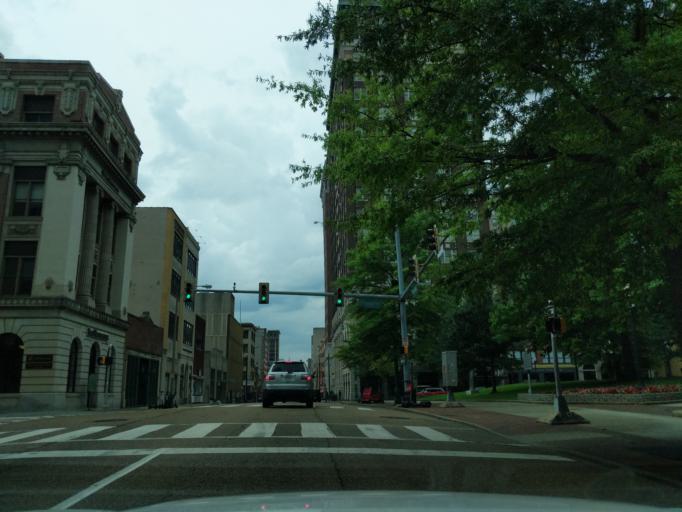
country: US
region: Tennessee
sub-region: Shelby County
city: Memphis
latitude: 35.1461
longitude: -90.0511
